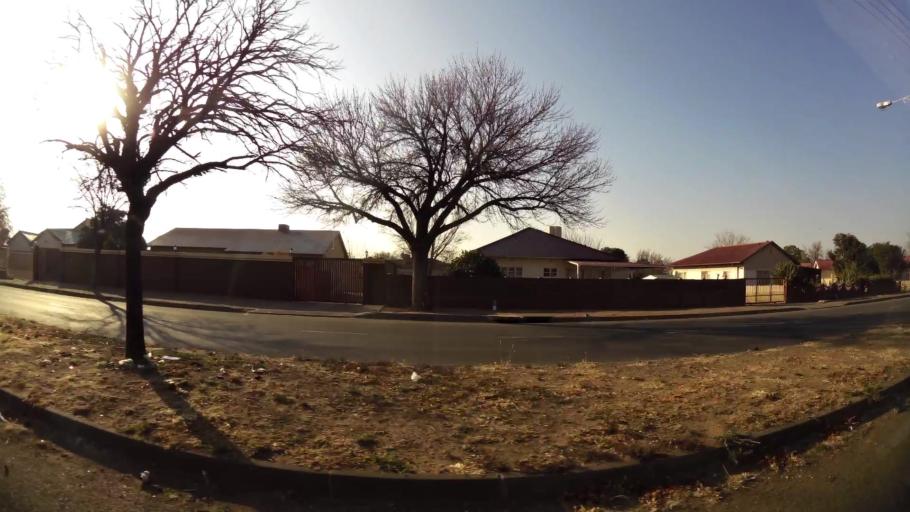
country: ZA
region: Orange Free State
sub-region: Mangaung Metropolitan Municipality
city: Bloemfontein
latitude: -29.1499
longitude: 26.2135
